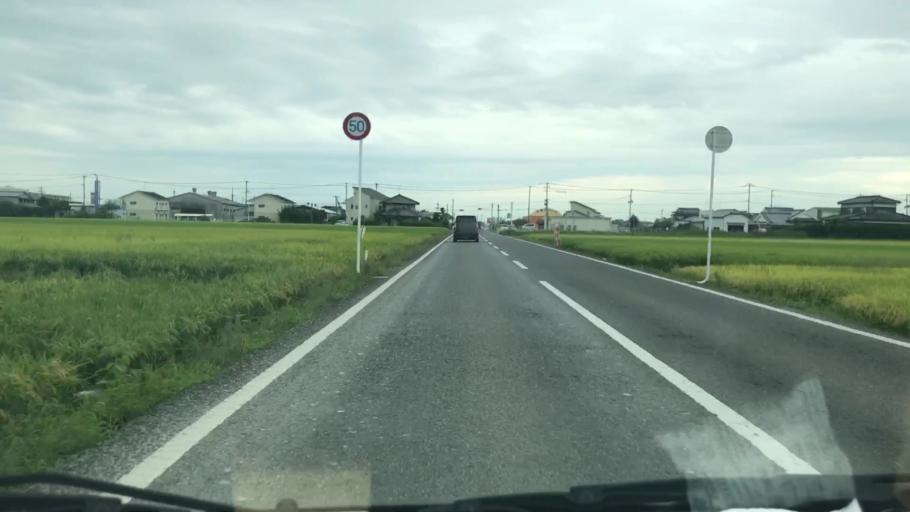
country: JP
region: Saga Prefecture
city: Saga-shi
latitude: 33.2279
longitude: 130.2914
